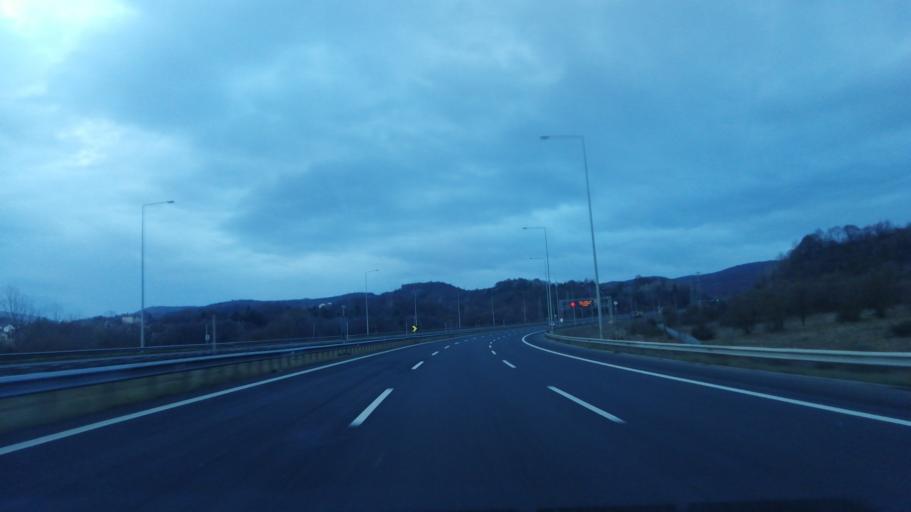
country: TR
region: Duzce
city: Kaynasli
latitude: 40.7246
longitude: 31.4486
